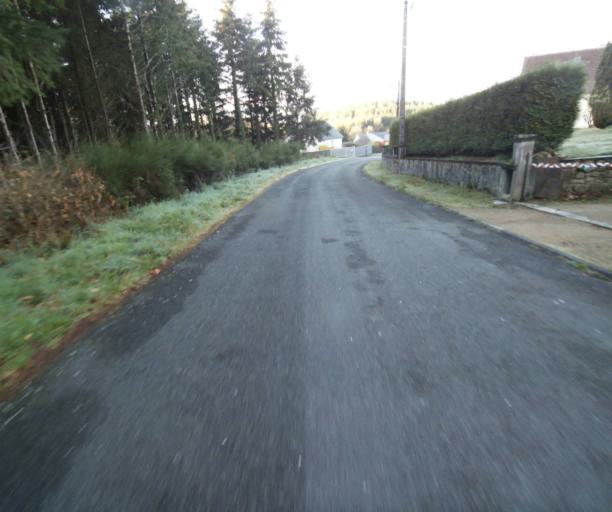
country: FR
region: Limousin
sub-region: Departement de la Correze
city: Correze
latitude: 45.3166
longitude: 1.8448
